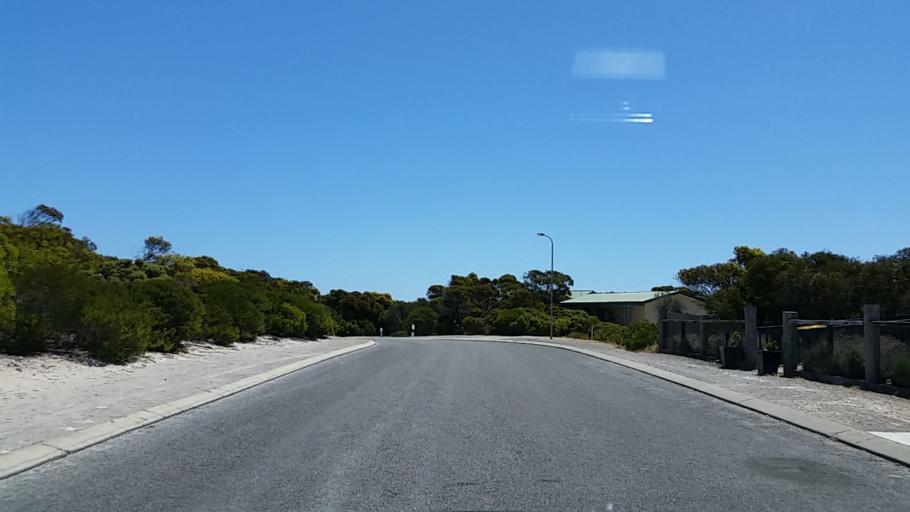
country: AU
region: South Australia
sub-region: Yorke Peninsula
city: Honiton
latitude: -35.2485
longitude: 136.9707
